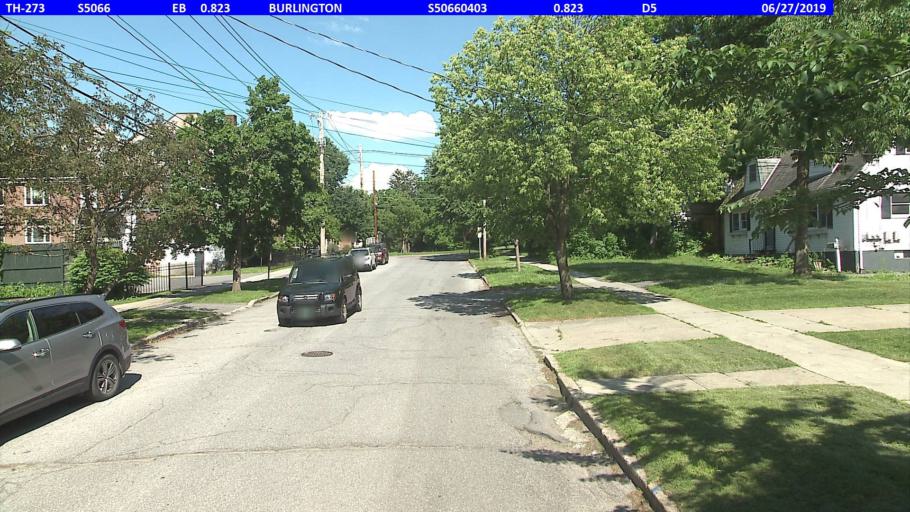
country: US
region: Vermont
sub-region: Chittenden County
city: Burlington
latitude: 44.4741
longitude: -73.2016
